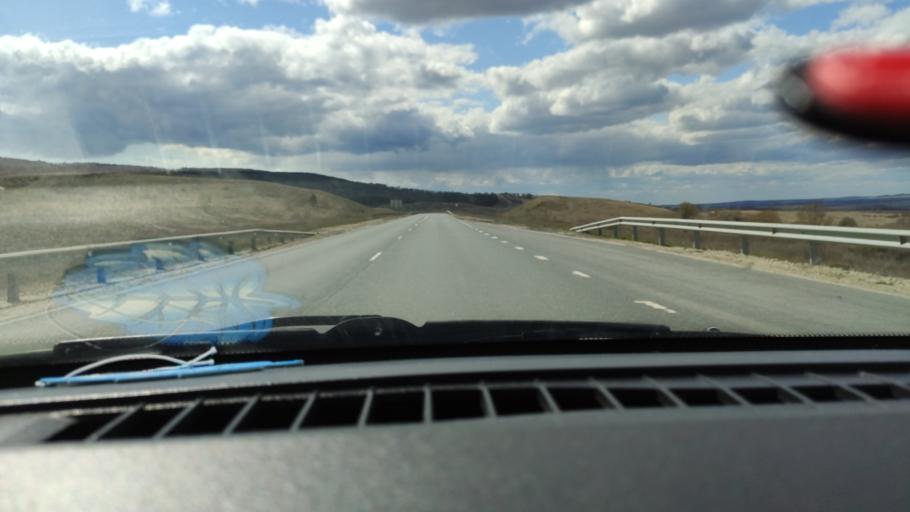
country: RU
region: Saratov
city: Alekseyevka
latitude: 52.3386
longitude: 47.9330
